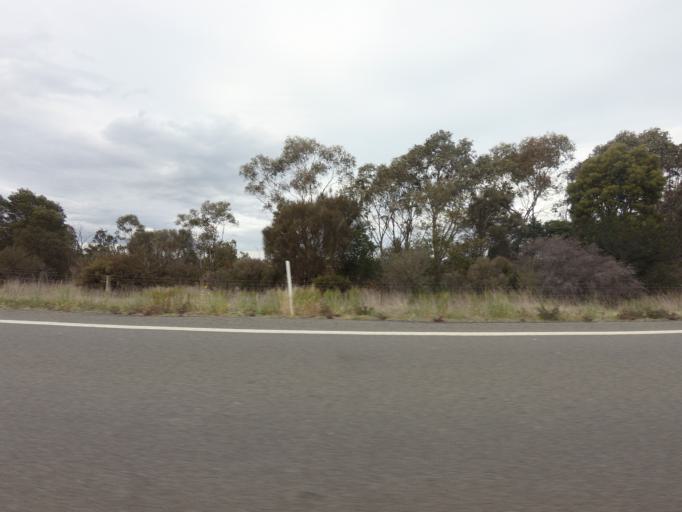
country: AU
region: Tasmania
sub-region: Break O'Day
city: St Helens
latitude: -42.1074
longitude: 148.0566
